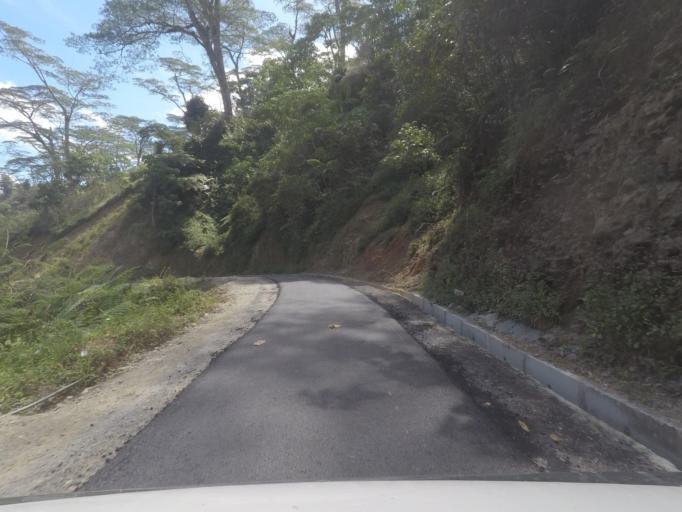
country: TL
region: Ermera
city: Gleno
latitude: -8.7532
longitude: 125.3341
